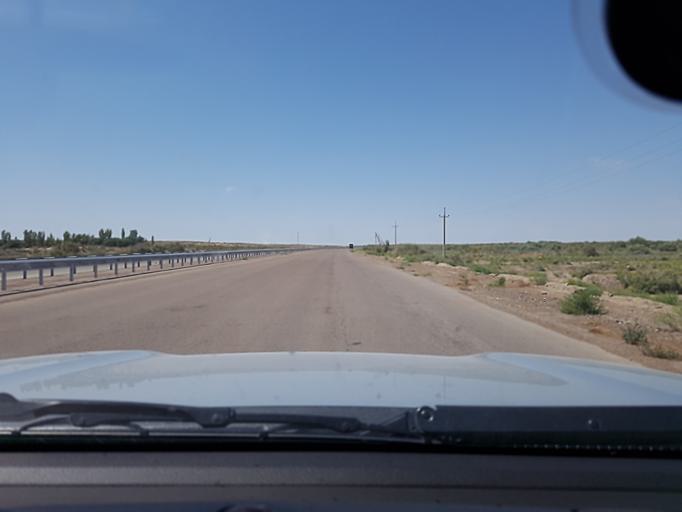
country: TM
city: Akdepe
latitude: 41.7503
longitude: 59.3142
